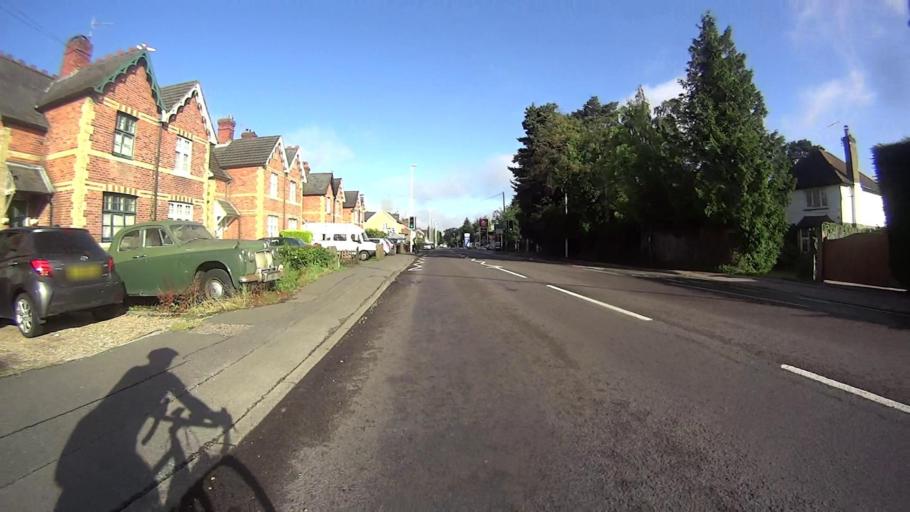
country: GB
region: England
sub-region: Surrey
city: Felbridge
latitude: 51.1360
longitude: -0.0315
